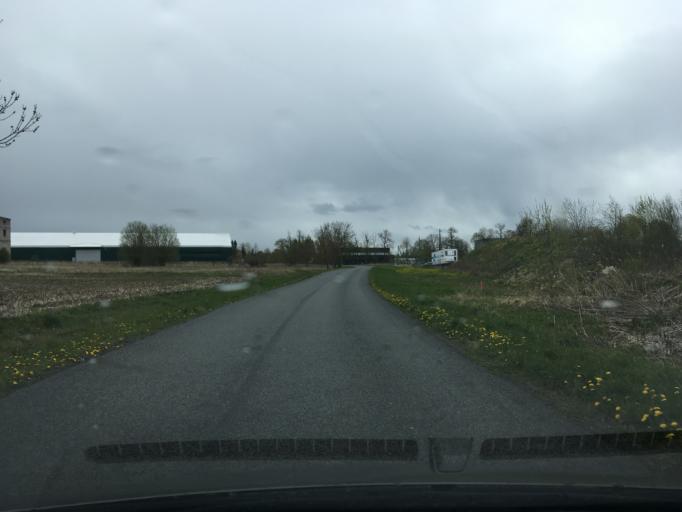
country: EE
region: Harju
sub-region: Rae vald
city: Vaida
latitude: 59.2950
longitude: 24.9724
